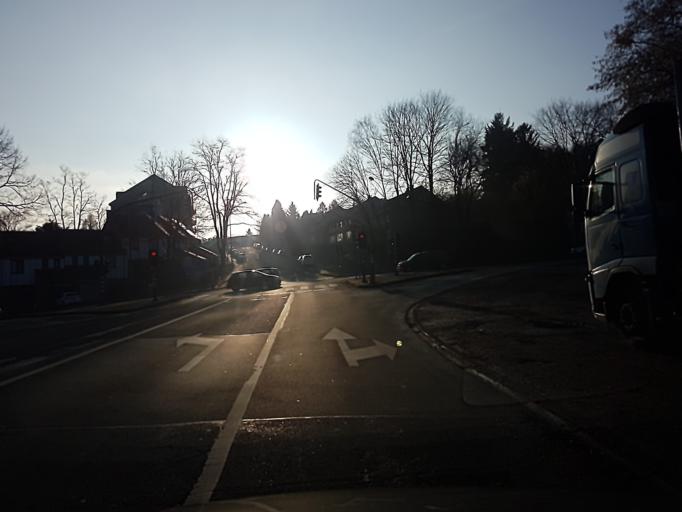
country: BE
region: Wallonia
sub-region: Province de Liege
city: Verviers
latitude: 50.5853
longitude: 5.8743
